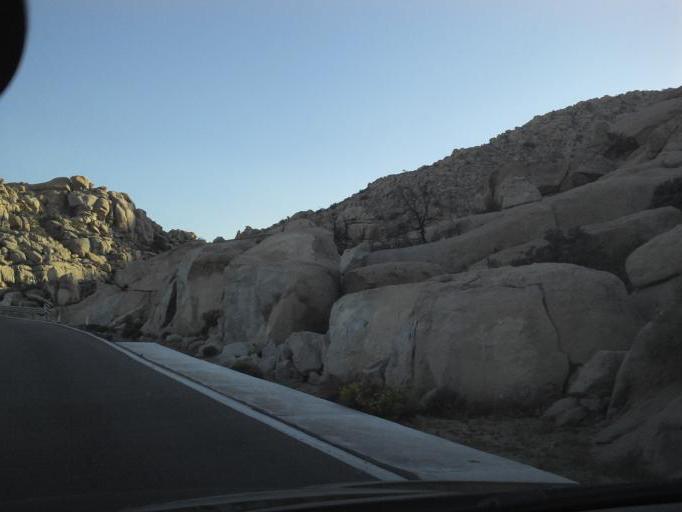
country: MX
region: Baja California
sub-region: Tecate
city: Cereso del Hongo
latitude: 32.5758
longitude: -116.0255
